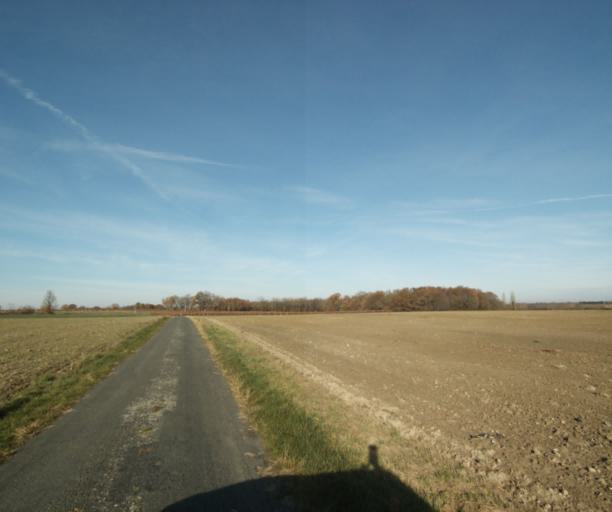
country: FR
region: Poitou-Charentes
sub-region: Departement de la Charente-Maritime
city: Cherac
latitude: 45.7483
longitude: -0.4804
